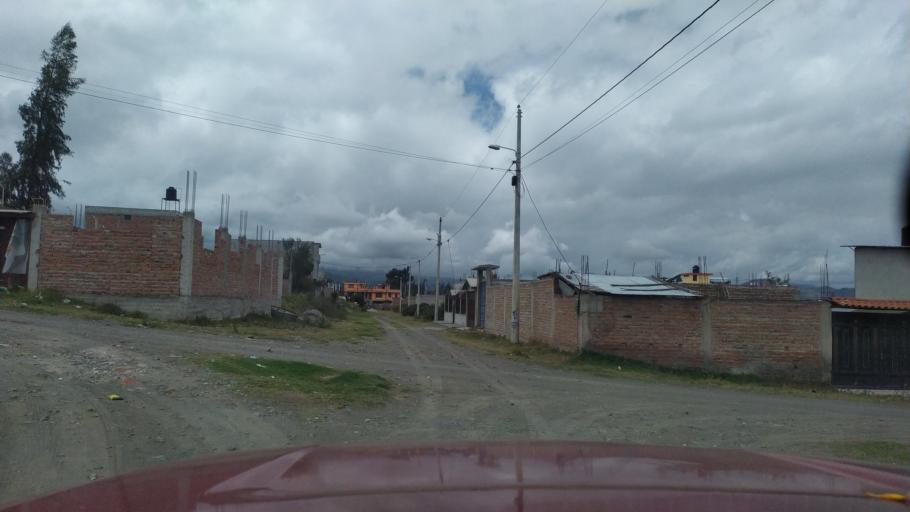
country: EC
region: Chimborazo
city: Riobamba
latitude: -1.6585
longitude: -78.6364
